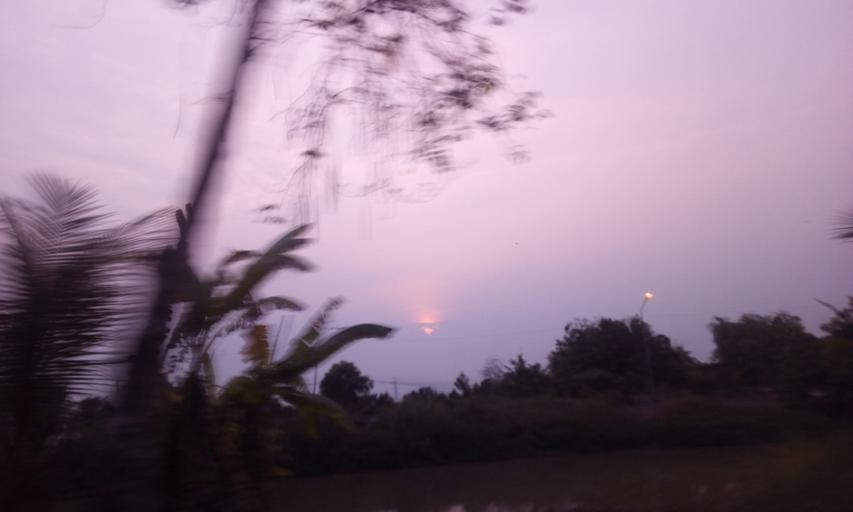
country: TH
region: Pathum Thani
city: Nong Suea
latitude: 14.0294
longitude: 100.8939
